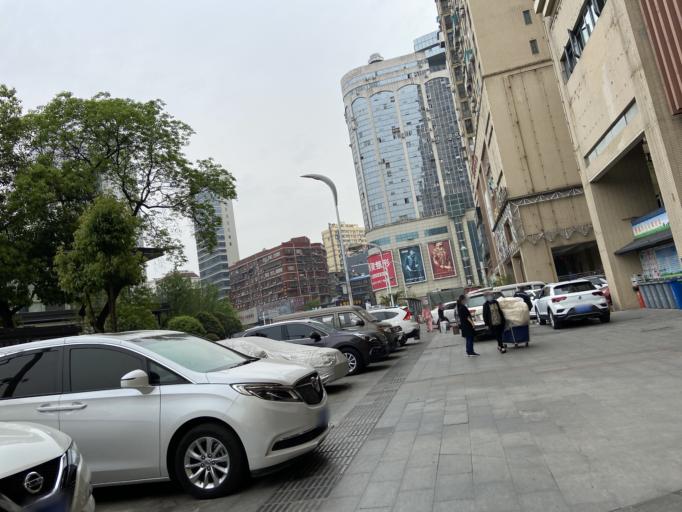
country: CN
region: Hubei
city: Yichang
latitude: 30.6994
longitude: 111.2781
